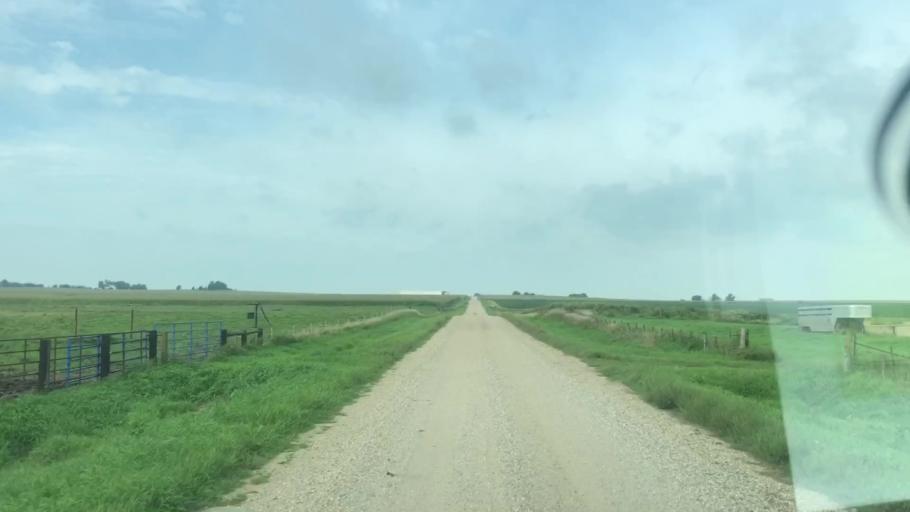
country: US
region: Iowa
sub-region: Lyon County
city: George
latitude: 43.2724
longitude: -95.9815
